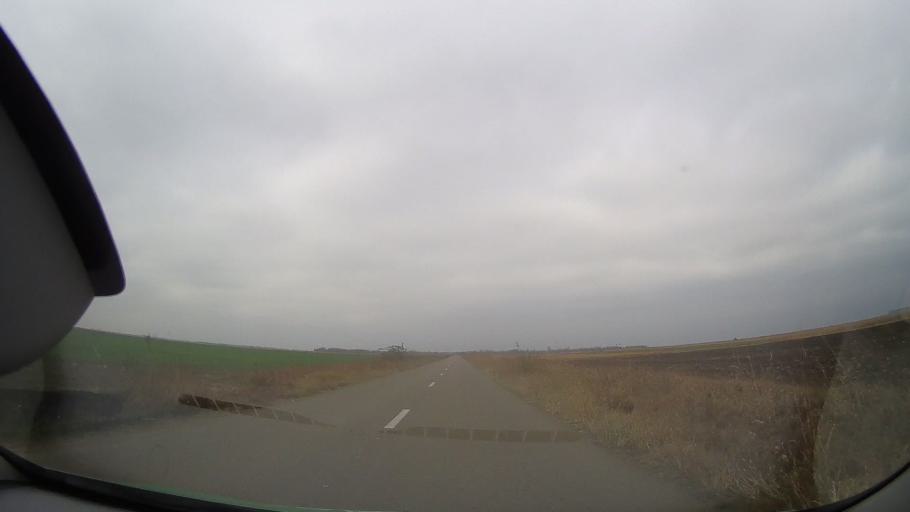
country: RO
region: Buzau
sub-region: Comuna Scutelnici
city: Scutelnici
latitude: 44.8633
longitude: 26.8973
